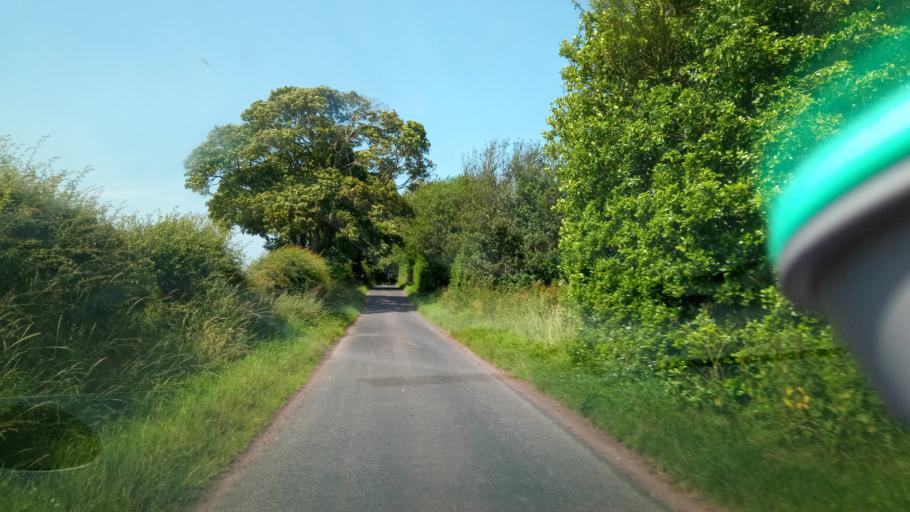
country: GB
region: Scotland
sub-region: The Scottish Borders
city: Jedburgh
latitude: 55.5362
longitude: -2.5676
